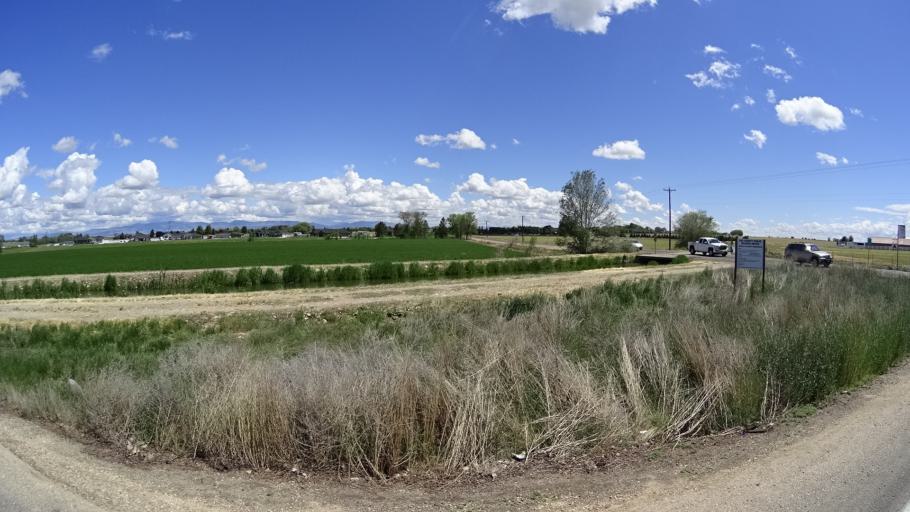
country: US
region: Idaho
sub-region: Ada County
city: Meridian
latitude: 43.5761
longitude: -116.4736
